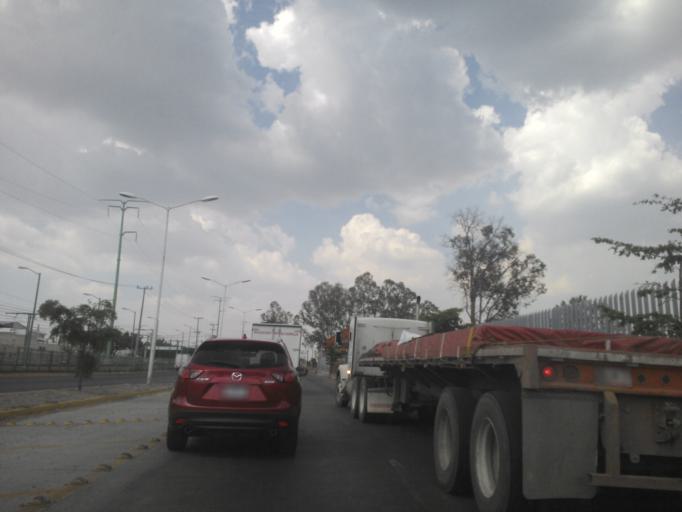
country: MX
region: Jalisco
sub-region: San Pedro Tlaquepaque
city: Paseo del Prado
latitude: 20.6090
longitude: -103.3993
